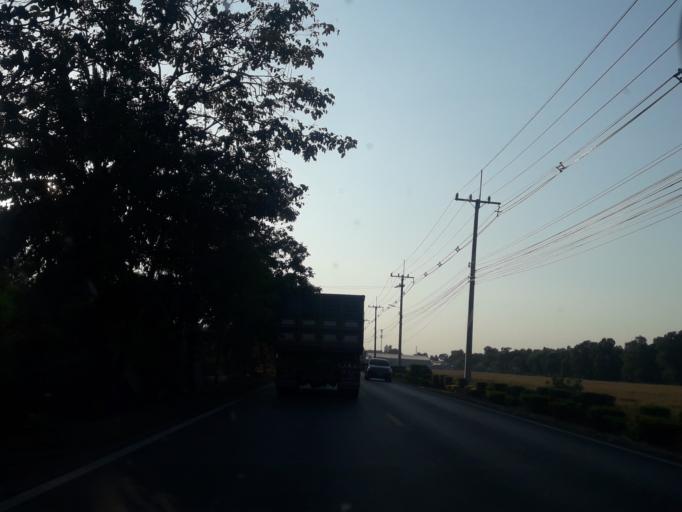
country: TH
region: Pathum Thani
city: Nong Suea
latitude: 14.1371
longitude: 100.8309
